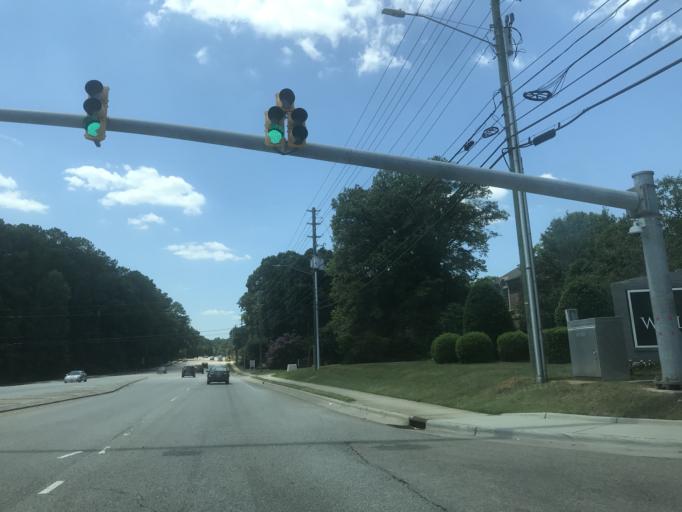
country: US
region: North Carolina
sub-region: Wake County
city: Cary
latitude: 35.7641
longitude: -78.7488
